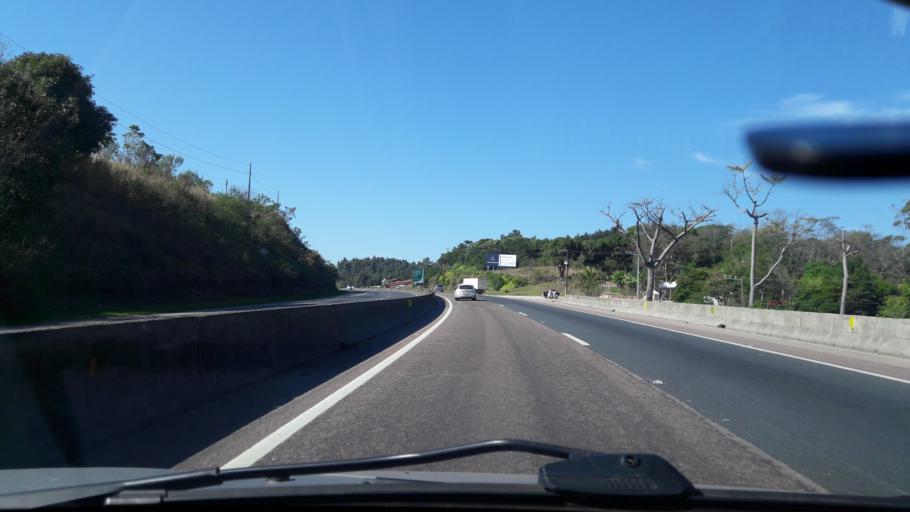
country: BR
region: Santa Catarina
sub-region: Tijucas
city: Tijucas
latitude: -27.3104
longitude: -48.6330
